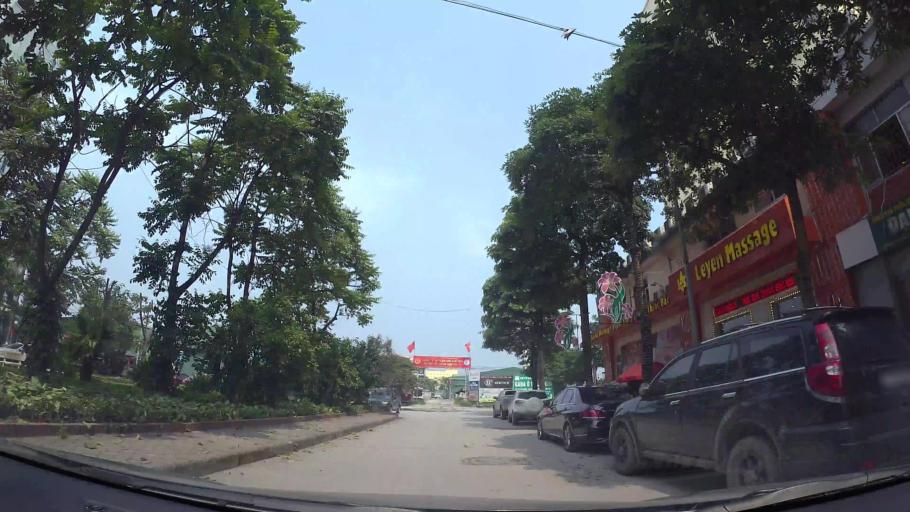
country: VN
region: Ha Noi
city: Van Dien
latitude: 20.9755
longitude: 105.8367
